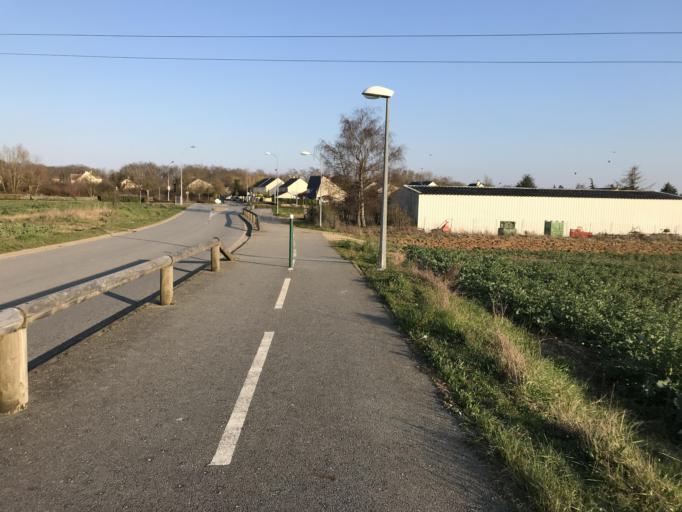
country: FR
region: Ile-de-France
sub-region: Departement de l'Essonne
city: Villejust
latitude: 48.6790
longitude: 2.2383
